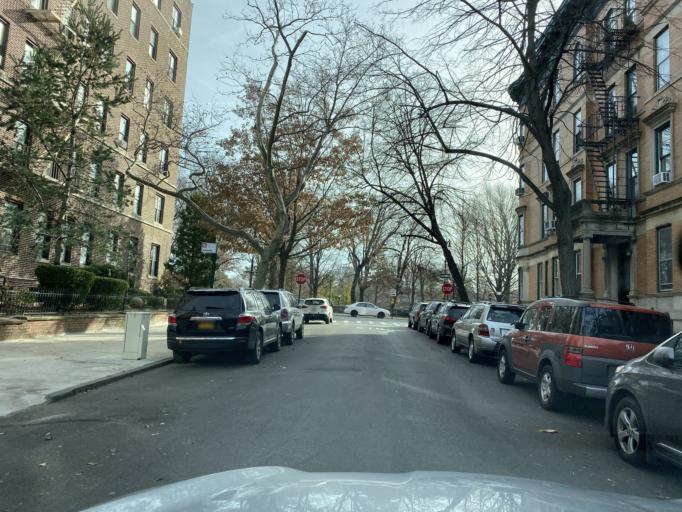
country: US
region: New York
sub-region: Kings County
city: Brooklyn
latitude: 40.6643
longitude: -73.9779
